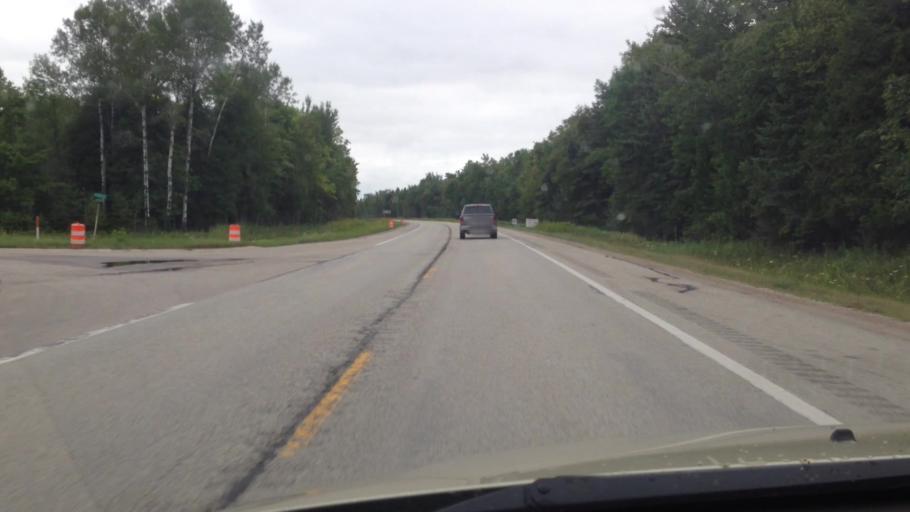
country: US
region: Michigan
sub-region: Delta County
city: Escanaba
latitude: 45.5841
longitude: -87.2407
